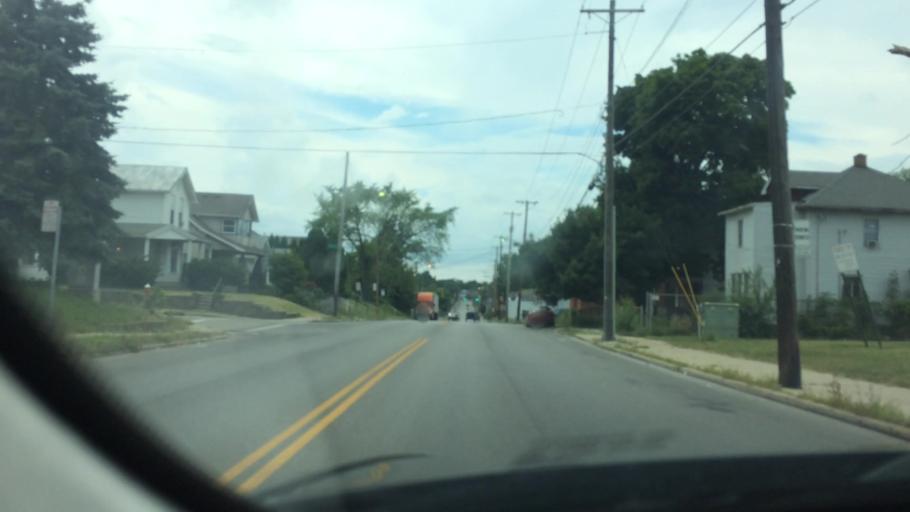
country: US
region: Ohio
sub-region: Wood County
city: Rossford
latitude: 41.6347
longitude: -83.5718
